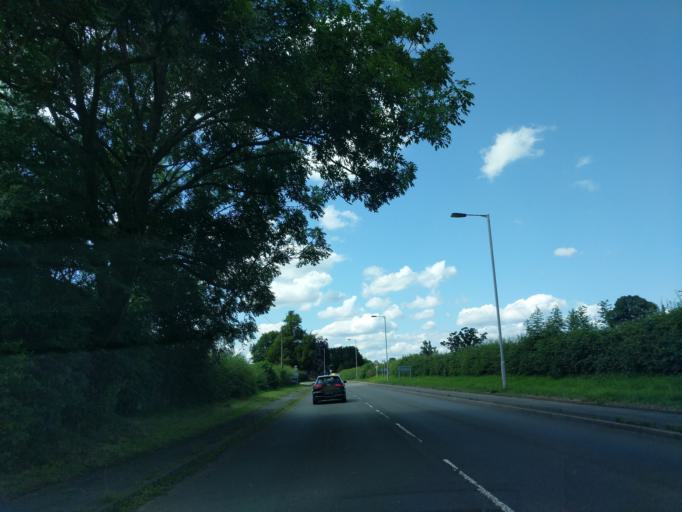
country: GB
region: England
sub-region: Staffordshire
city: Cheadle
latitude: 52.9430
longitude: -1.9689
